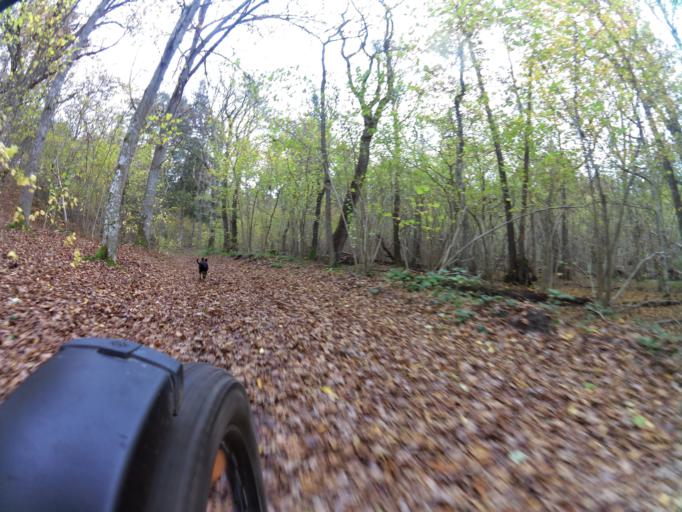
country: PL
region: Pomeranian Voivodeship
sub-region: Powiat pucki
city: Krokowa
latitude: 54.8306
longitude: 18.1154
